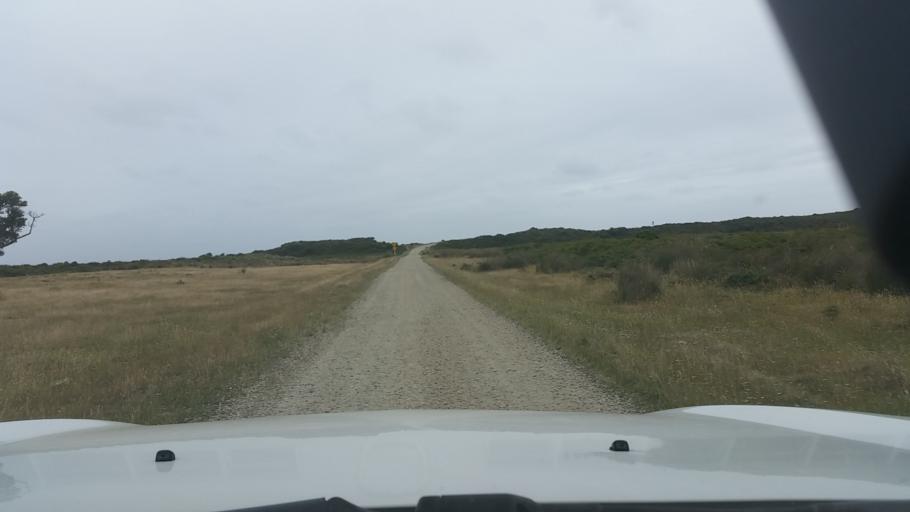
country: NZ
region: Chatham Islands
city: Waitangi
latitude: -43.7689
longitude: -176.3197
